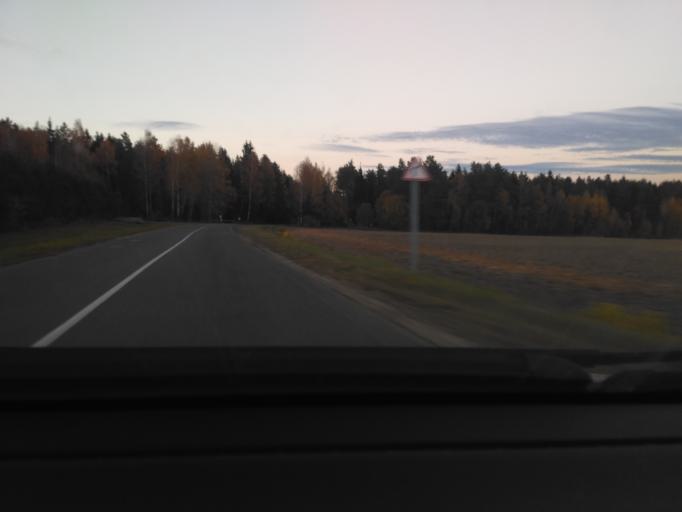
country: BY
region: Minsk
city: Loshnitsa
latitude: 54.3696
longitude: 28.6233
